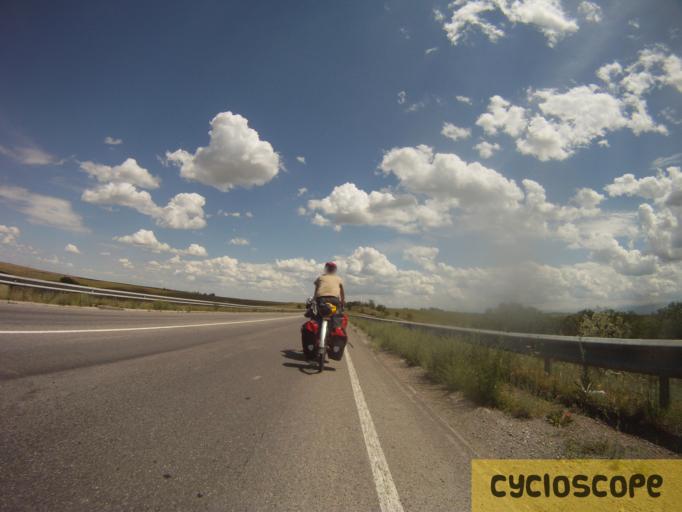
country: KG
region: Chuy
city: Bystrovka
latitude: 43.3149
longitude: 76.1366
